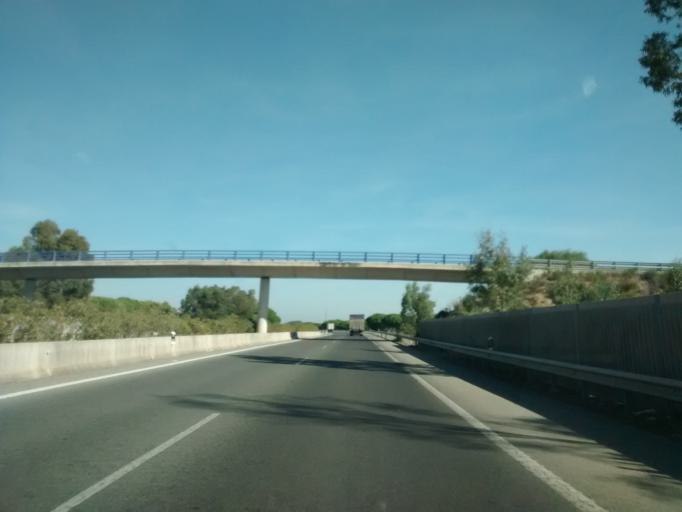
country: ES
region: Andalusia
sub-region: Provincia de Cadiz
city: Chiclana de la Frontera
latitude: 36.3792
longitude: -6.1143
